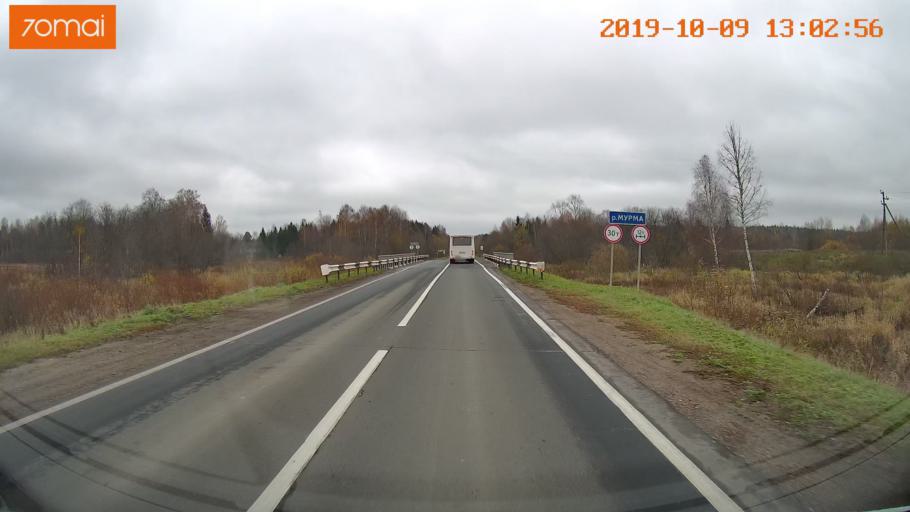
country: RU
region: Jaroslavl
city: Lyubim
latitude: 58.3598
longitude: 40.5138
